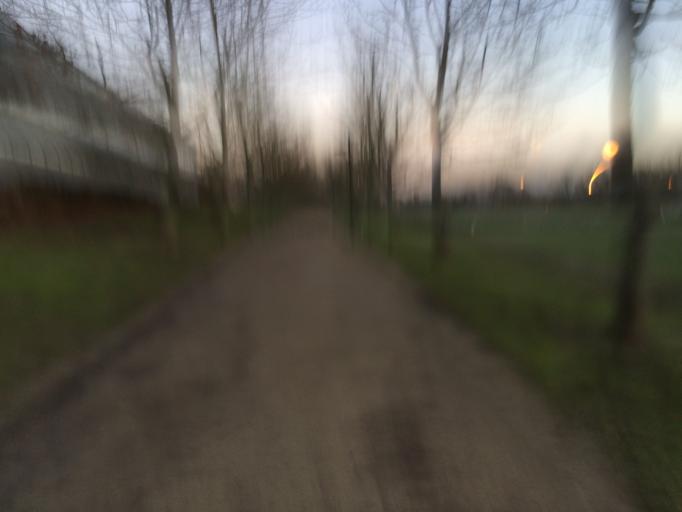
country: FR
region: Ile-de-France
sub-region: Departement des Hauts-de-Seine
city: Sceaux
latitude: 48.7701
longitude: 2.2851
